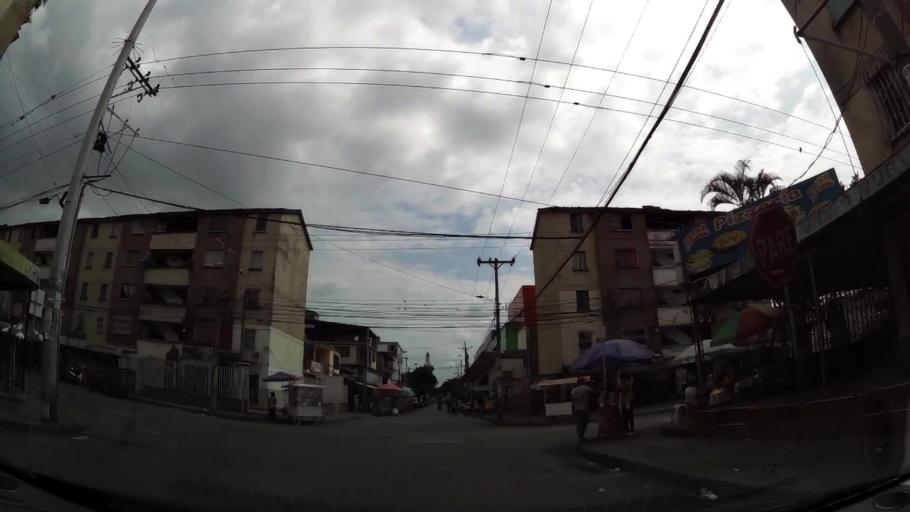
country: CO
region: Valle del Cauca
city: Cali
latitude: 3.4856
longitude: -76.4891
